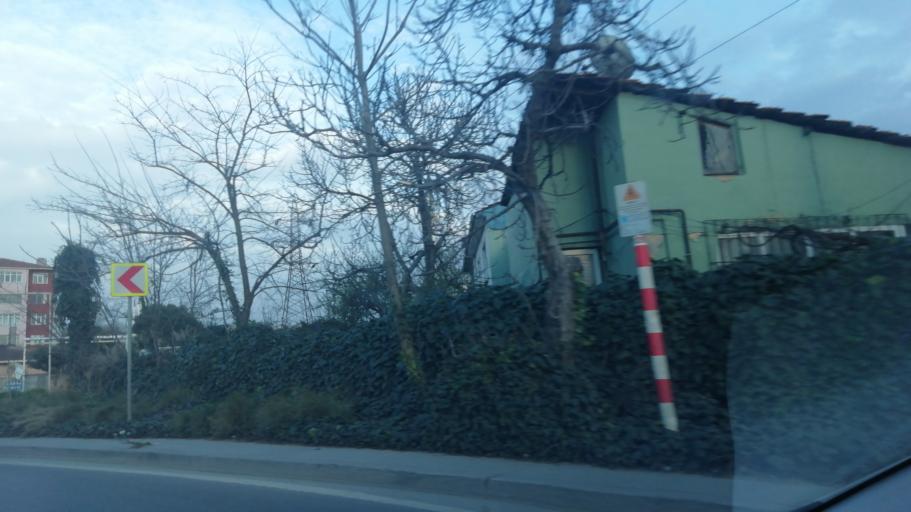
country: TR
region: Istanbul
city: Mahmutbey
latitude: 40.9849
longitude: 28.7684
